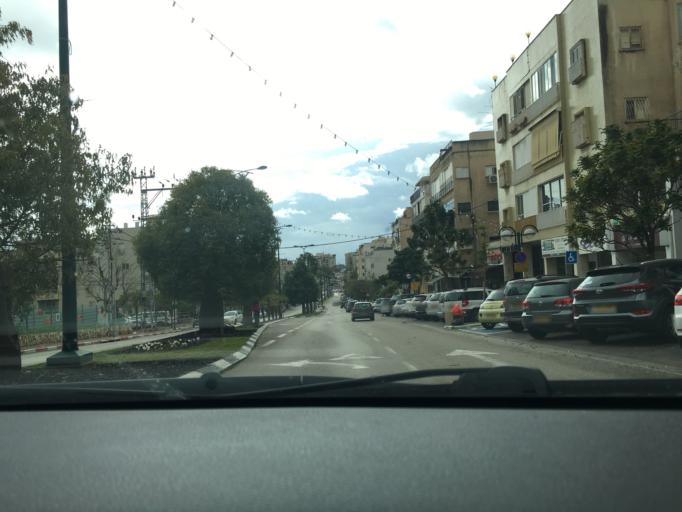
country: IL
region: Tel Aviv
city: Ramat HaSharon
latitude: 32.1408
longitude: 34.8427
